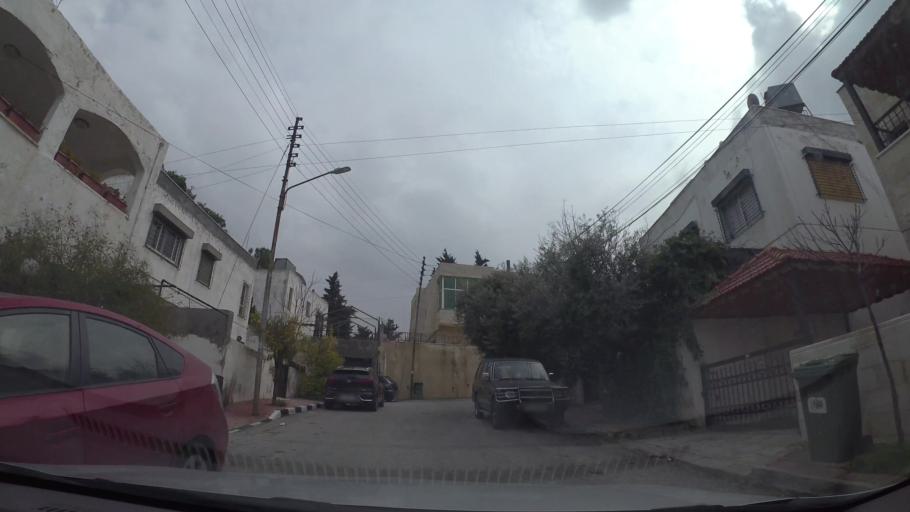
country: JO
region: Amman
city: Umm as Summaq
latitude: 31.8955
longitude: 35.8595
